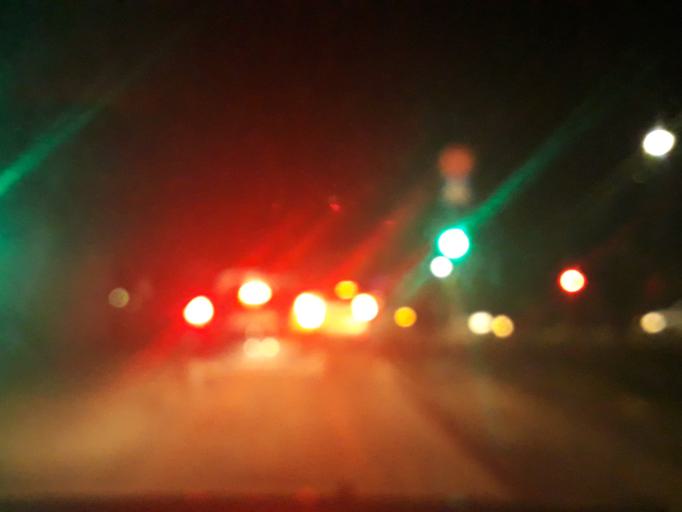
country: BA
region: Federation of Bosnia and Herzegovina
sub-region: Kanton Sarajevo
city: Sarajevo
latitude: 43.8354
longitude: 18.3427
